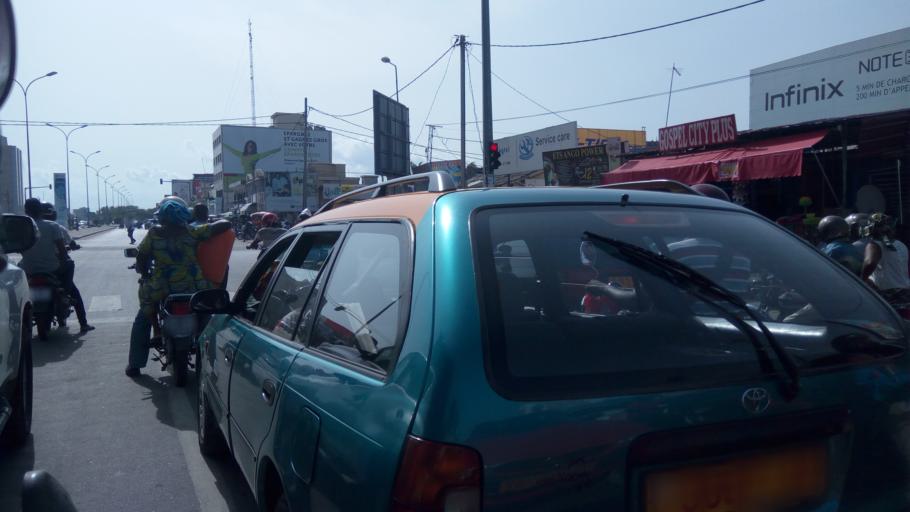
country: TG
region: Maritime
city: Lome
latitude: 6.1359
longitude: 1.2291
